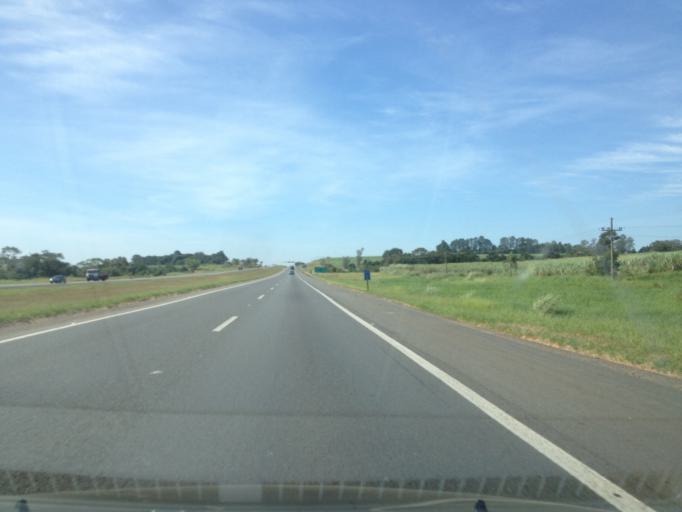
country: BR
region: Sao Paulo
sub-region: Tatui
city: Tatui
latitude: -23.2555
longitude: -47.9177
